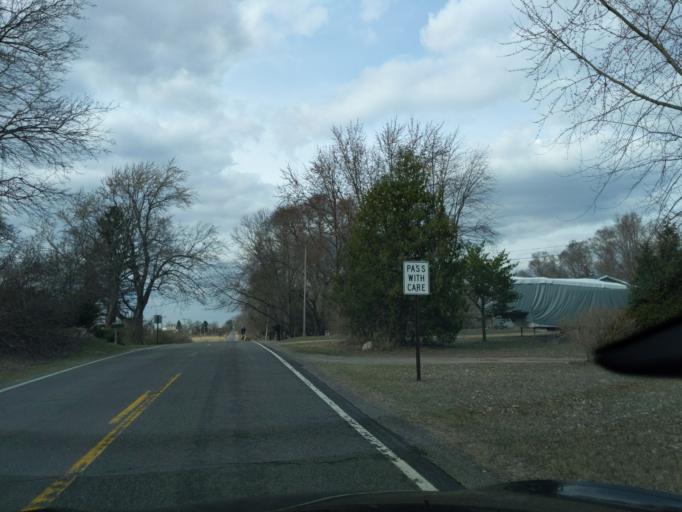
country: US
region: Michigan
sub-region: Ingham County
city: Mason
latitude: 42.5425
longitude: -84.4831
